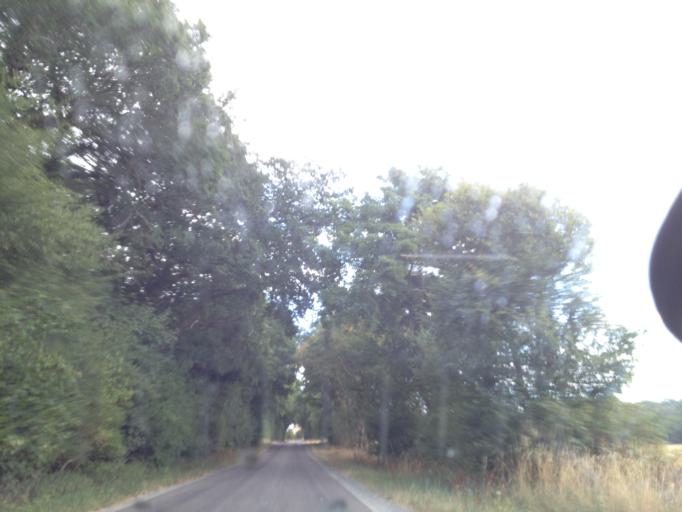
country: DK
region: Zealand
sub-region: Guldborgsund Kommune
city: Sakskobing
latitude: 54.7798
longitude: 11.6564
